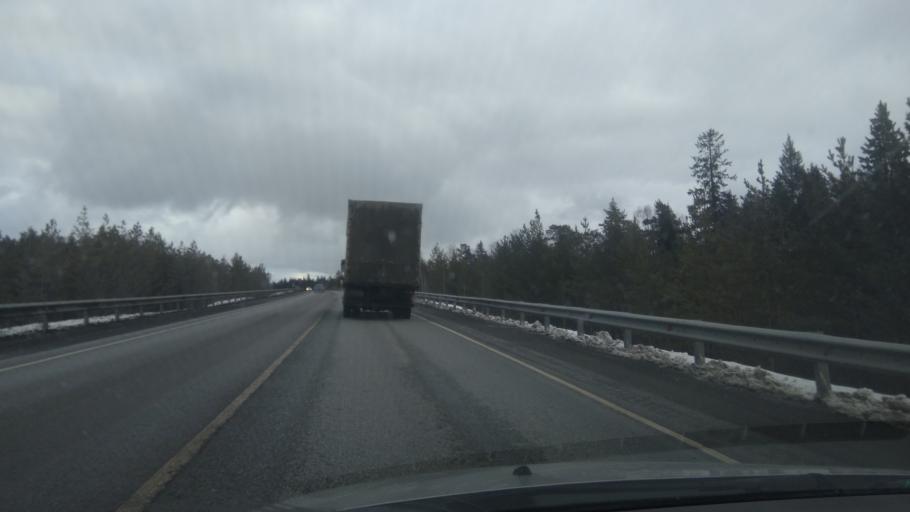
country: RU
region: Sverdlovsk
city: Atig
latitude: 56.7961
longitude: 59.4036
